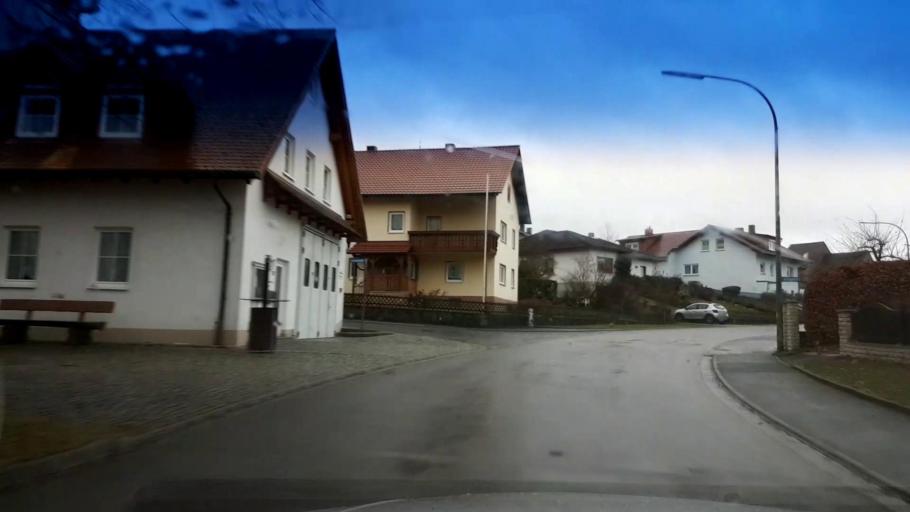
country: DE
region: Bavaria
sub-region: Upper Franconia
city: Litzendorf
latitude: 49.8729
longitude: 11.0449
